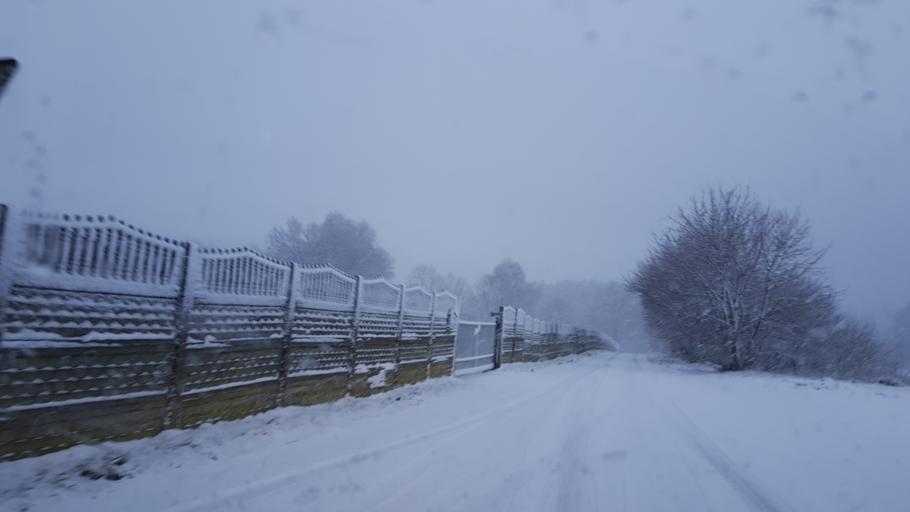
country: PL
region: West Pomeranian Voivodeship
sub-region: Powiat koszalinski
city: Polanow
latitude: 54.1864
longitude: 16.5177
